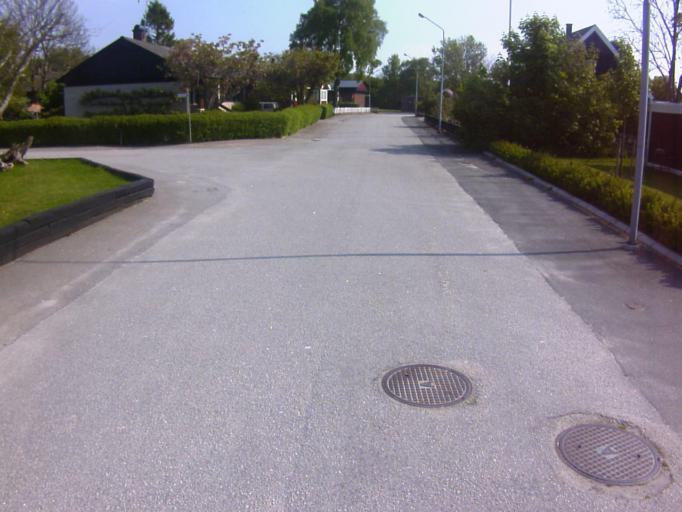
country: SE
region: Blekinge
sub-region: Solvesborgs Kommun
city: Soelvesborg
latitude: 56.0061
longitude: 14.7312
